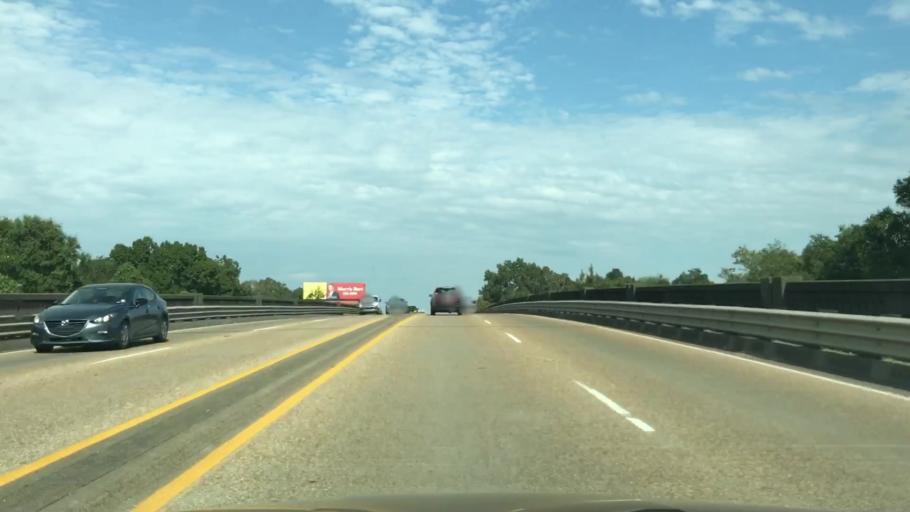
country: US
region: Louisiana
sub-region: Jefferson Parish
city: Bridge City
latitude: 29.9150
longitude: -90.1741
